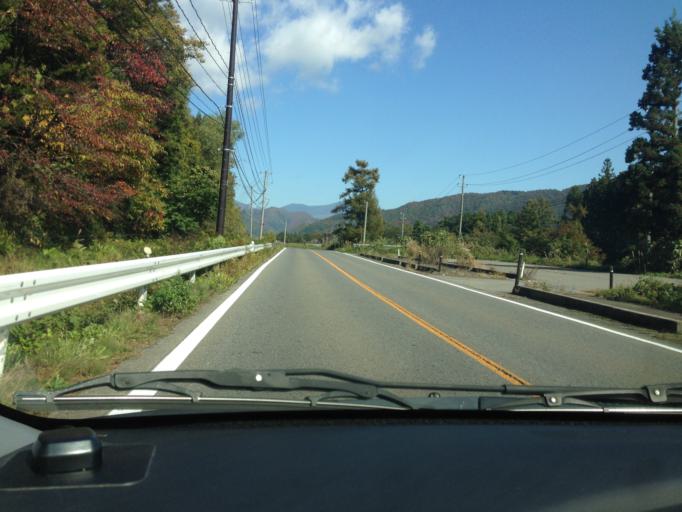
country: JP
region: Fukushima
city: Inawashiro
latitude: 37.5834
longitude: 140.1236
